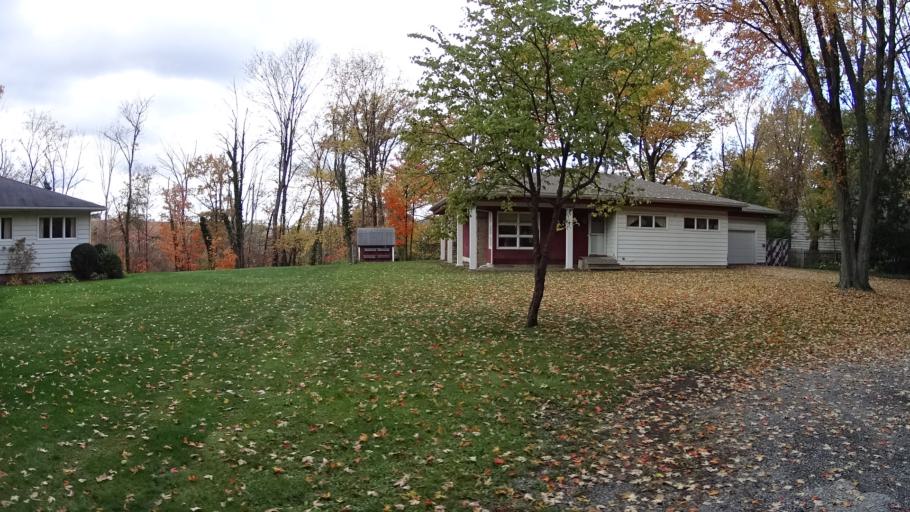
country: US
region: Ohio
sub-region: Lorain County
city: Amherst
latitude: 41.4202
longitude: -82.2068
